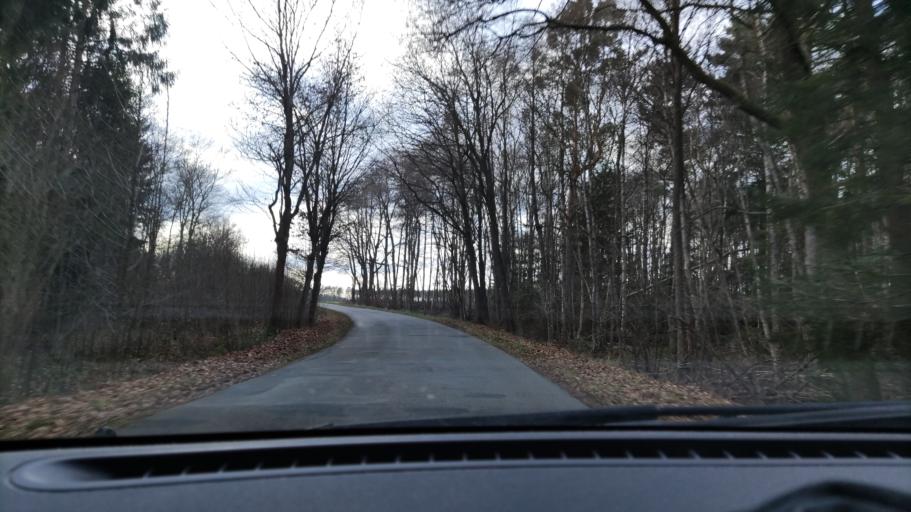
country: DE
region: Lower Saxony
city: Eimke
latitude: 52.9798
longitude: 10.3343
